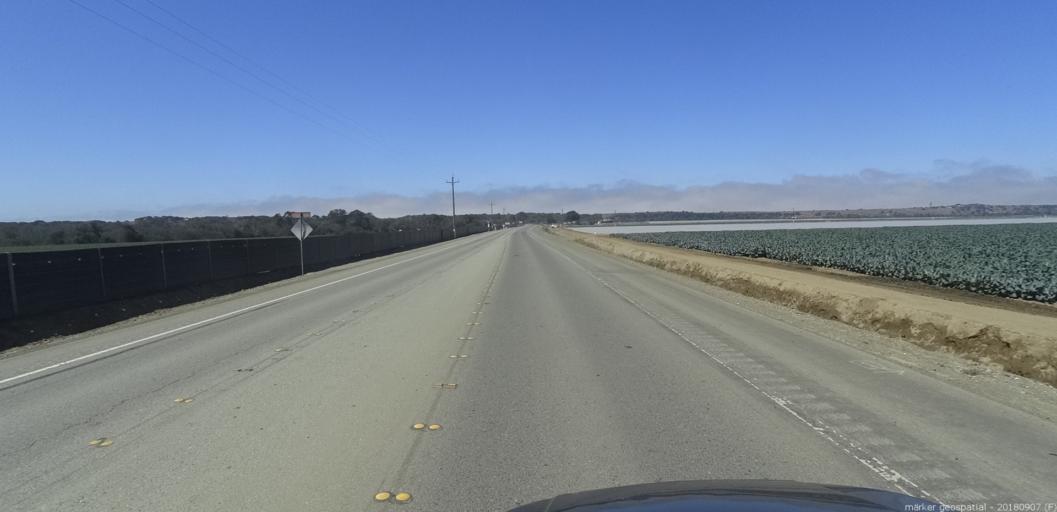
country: US
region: California
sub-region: Monterey County
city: Boronda
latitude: 36.6787
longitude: -121.7360
